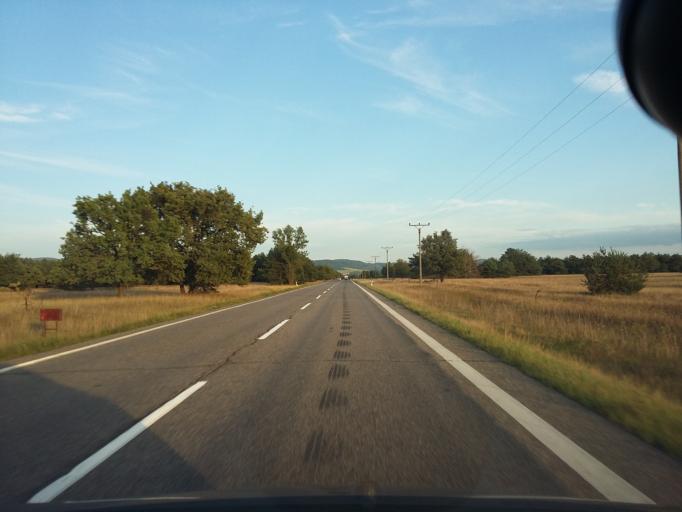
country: SK
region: Bratislavsky
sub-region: Okres Malacky
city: Malacky
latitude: 48.4170
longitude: 17.0604
